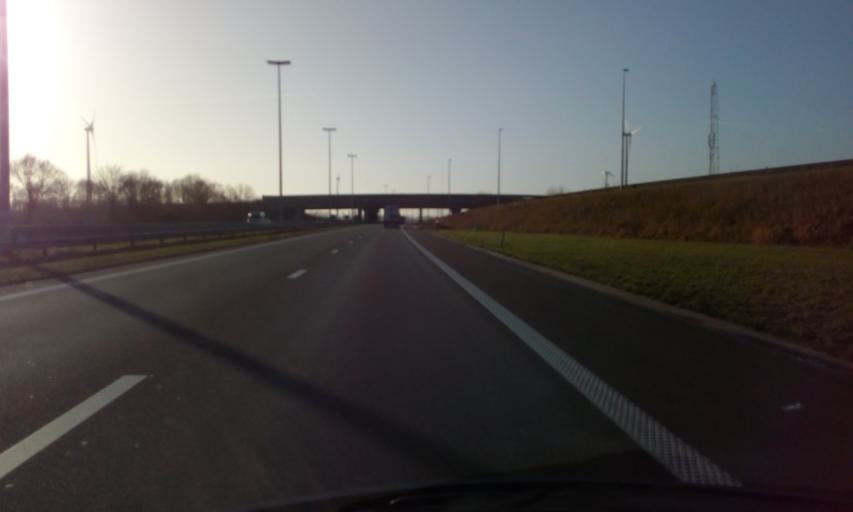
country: BE
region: Flanders
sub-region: Provincie Antwerpen
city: Hoogstraten
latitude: 51.4159
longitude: 4.7037
